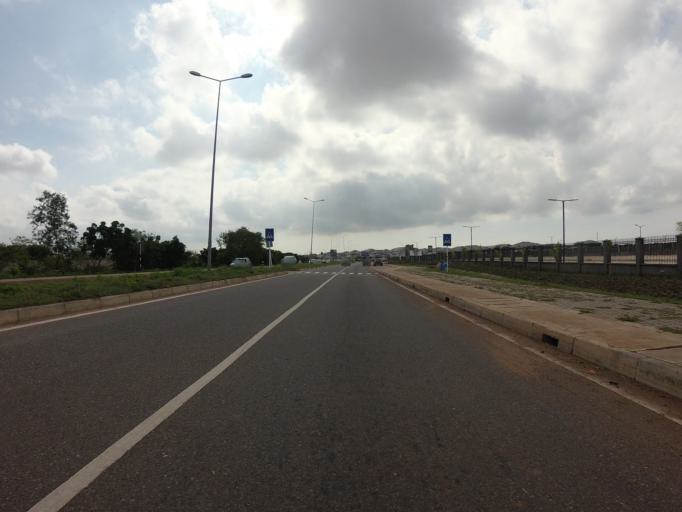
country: GH
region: Greater Accra
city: Teshi Old Town
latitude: 5.6110
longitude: -0.1471
